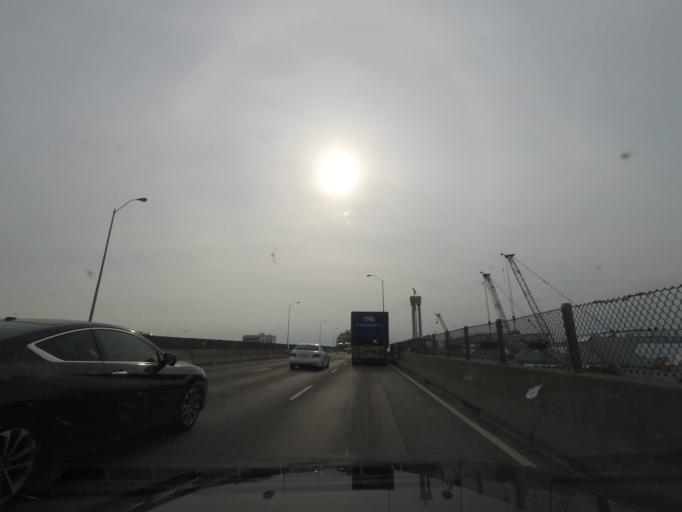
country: CA
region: Quebec
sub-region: Monteregie
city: Brossard
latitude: 45.4668
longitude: -73.4975
